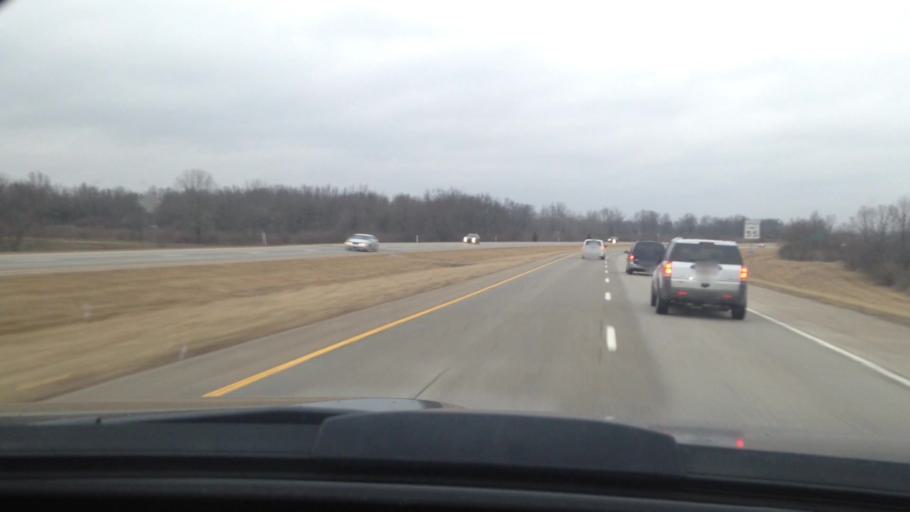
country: US
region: Indiana
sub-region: Delaware County
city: Muncie
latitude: 40.1587
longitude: -85.3534
